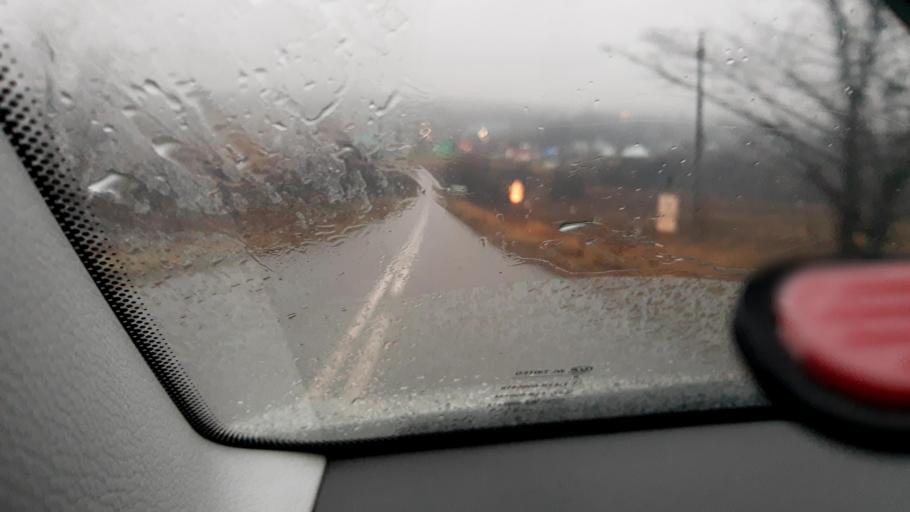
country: RU
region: Bashkortostan
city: Iglino
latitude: 54.8998
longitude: 56.2154
